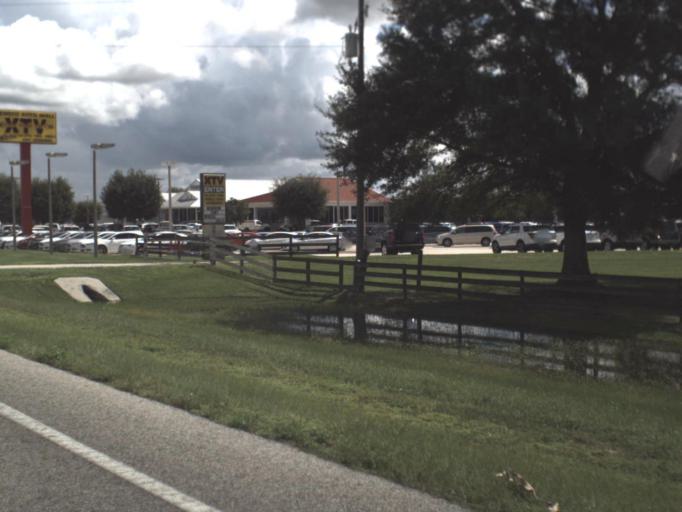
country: US
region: Florida
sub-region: DeSoto County
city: Arcadia
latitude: 27.2088
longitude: -81.8257
